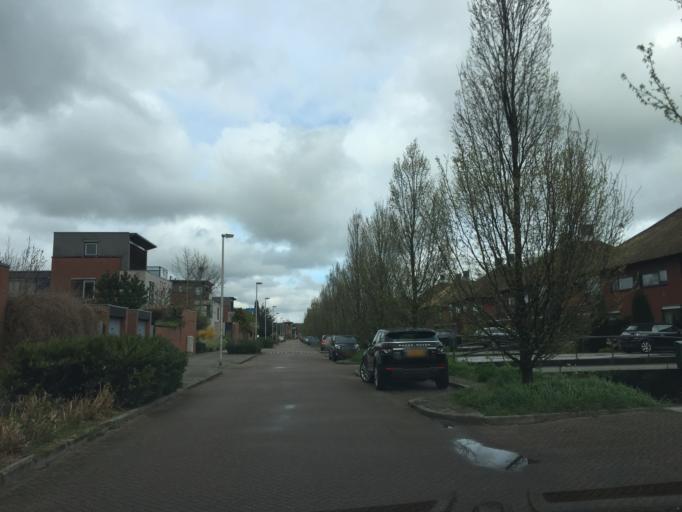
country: NL
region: South Holland
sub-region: Gemeente Leiderdorp
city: Leiderdorp
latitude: 52.1697
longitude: 4.5367
